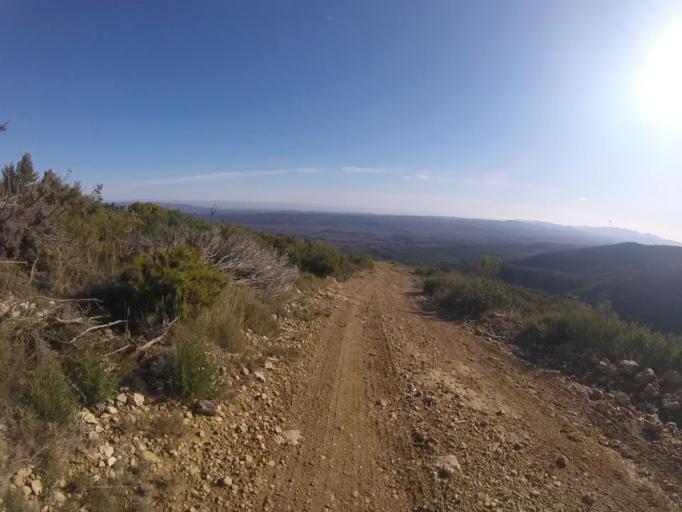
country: ES
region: Valencia
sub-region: Provincia de Castello
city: Sarratella
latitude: 40.3002
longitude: 0.0376
